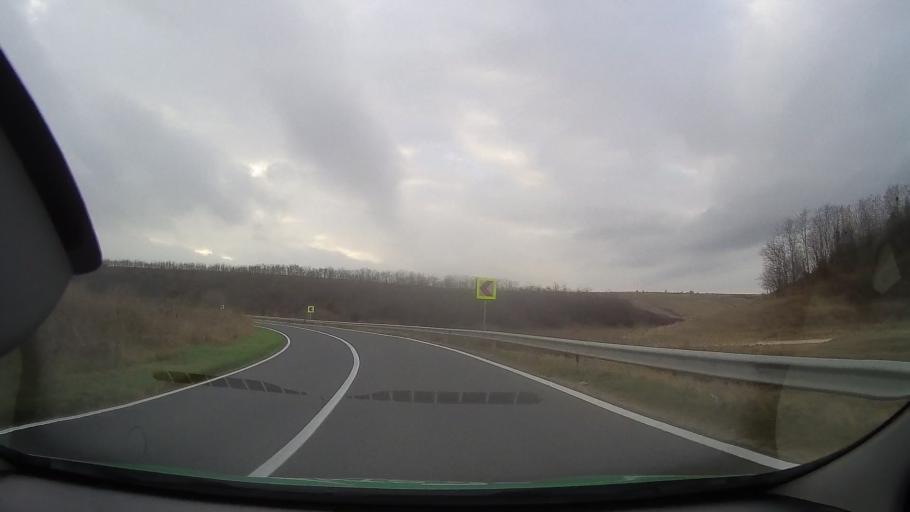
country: RO
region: Constanta
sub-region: Comuna Deleni
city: Deleni
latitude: 44.1025
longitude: 28.0259
